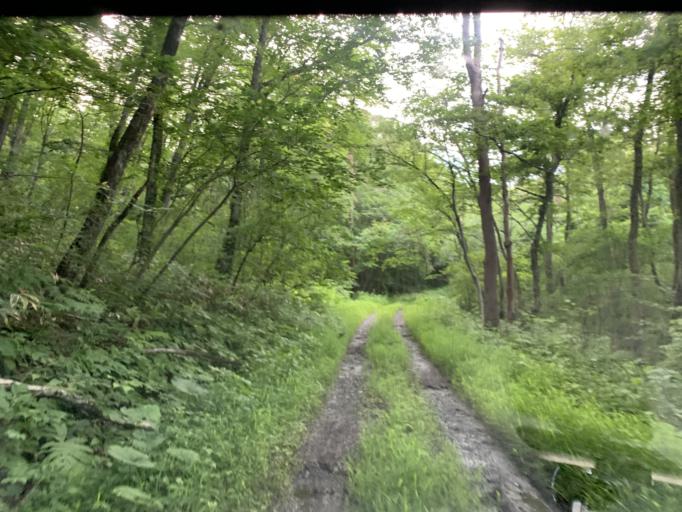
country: JP
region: Iwate
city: Ichinoseki
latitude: 38.9087
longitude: 140.9486
